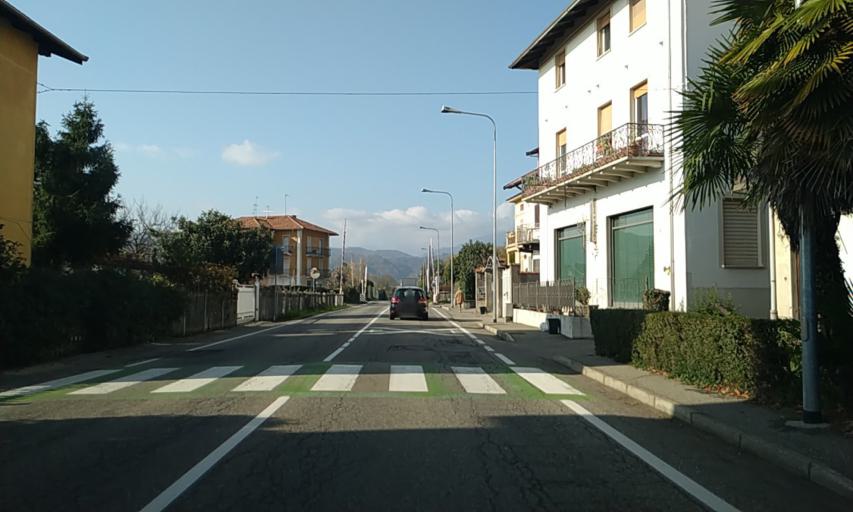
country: IT
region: Piedmont
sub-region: Provincia di Novara
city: Grignasco
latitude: 45.6840
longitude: 8.3325
